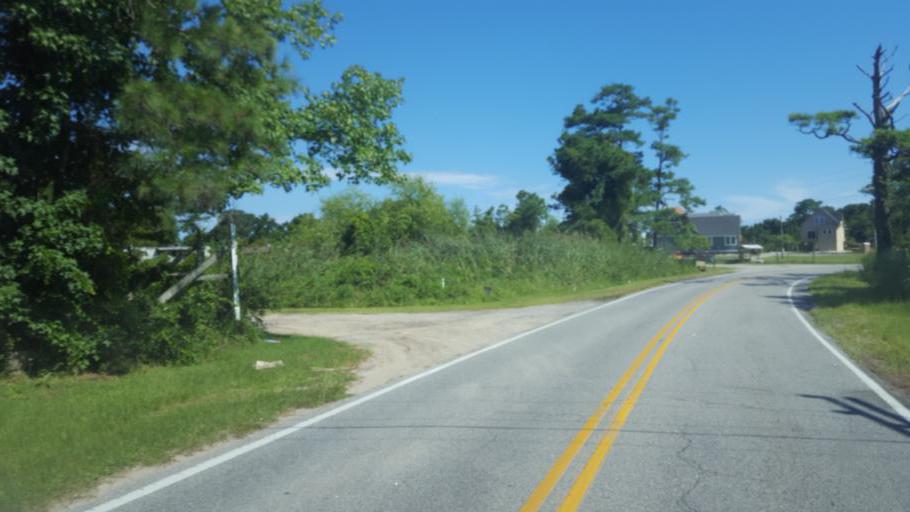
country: US
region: North Carolina
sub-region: Dare County
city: Kill Devil Hills
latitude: 36.0118
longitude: -75.6984
